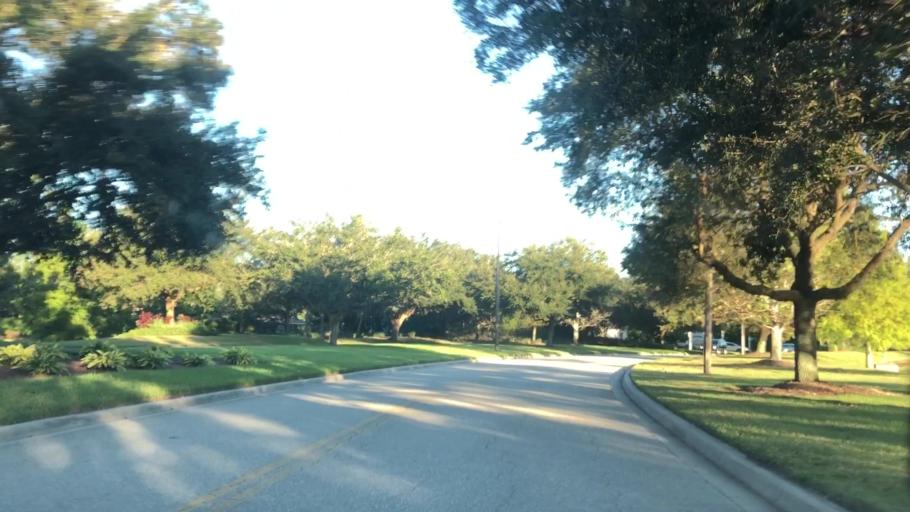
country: US
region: Florida
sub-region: Sarasota County
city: The Meadows
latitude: 27.4255
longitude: -82.4062
